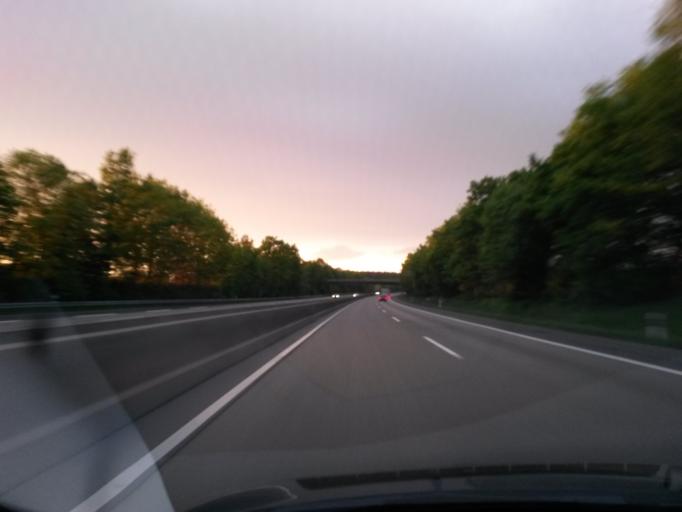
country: DE
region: Hesse
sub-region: Regierungsbezirk Kassel
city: Burghaun
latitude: 50.6650
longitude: 9.6767
